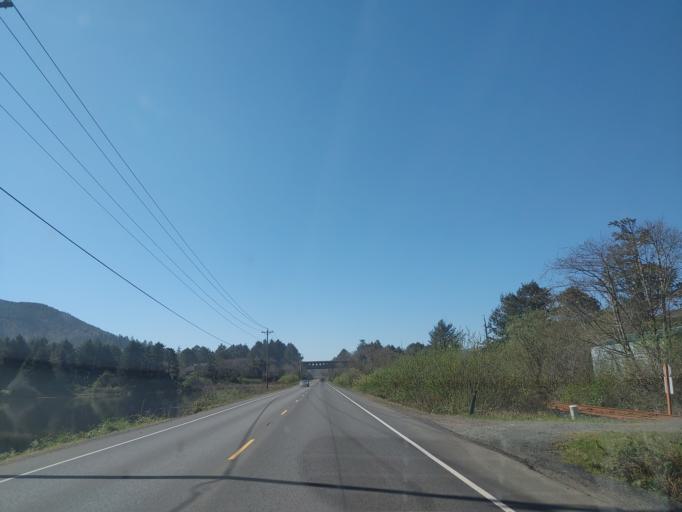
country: US
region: Oregon
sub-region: Tillamook County
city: Rockaway Beach
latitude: 45.5951
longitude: -123.9469
